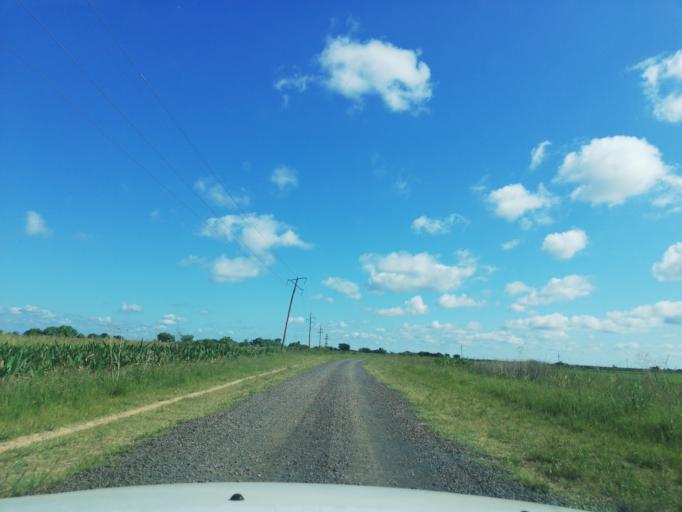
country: AR
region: Corrientes
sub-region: Departamento de San Miguel
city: San Miguel
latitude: -27.9752
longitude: -57.5809
